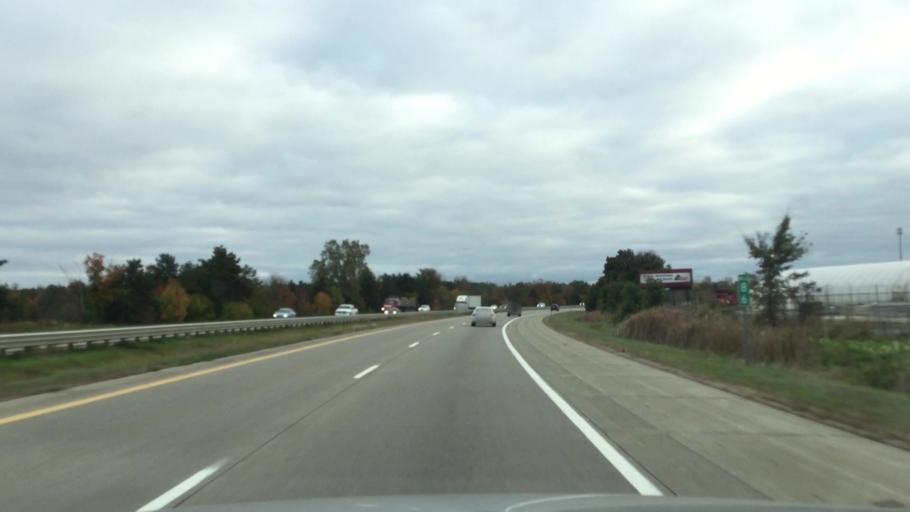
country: US
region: Michigan
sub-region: Genesee County
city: Lake Fenton
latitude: 42.8951
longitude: -83.7384
